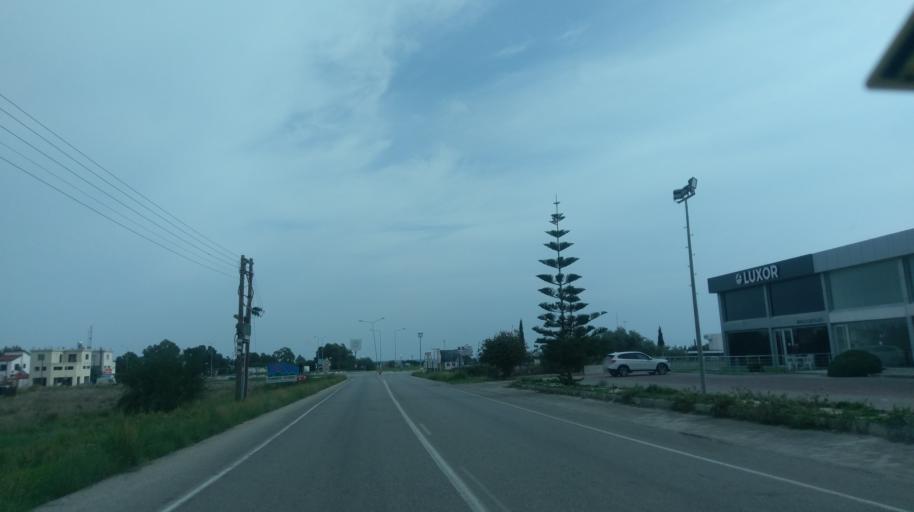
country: CY
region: Ammochostos
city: Trikomo
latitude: 35.2793
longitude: 33.9181
